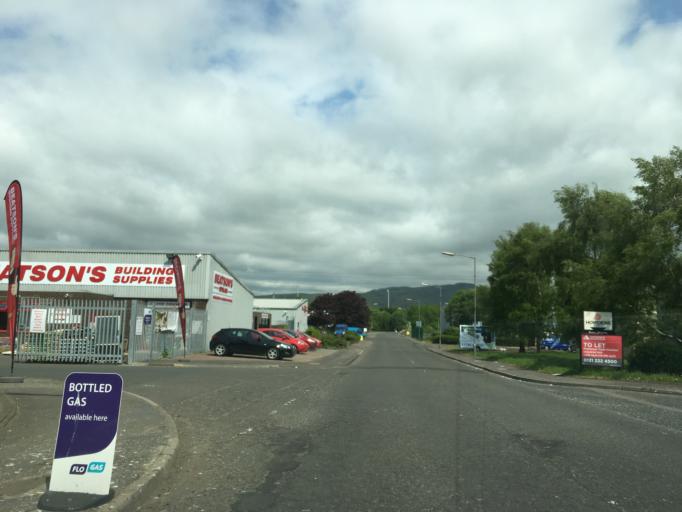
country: GB
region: Scotland
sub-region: Stirling
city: Stirling
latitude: 56.1143
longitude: -3.9138
